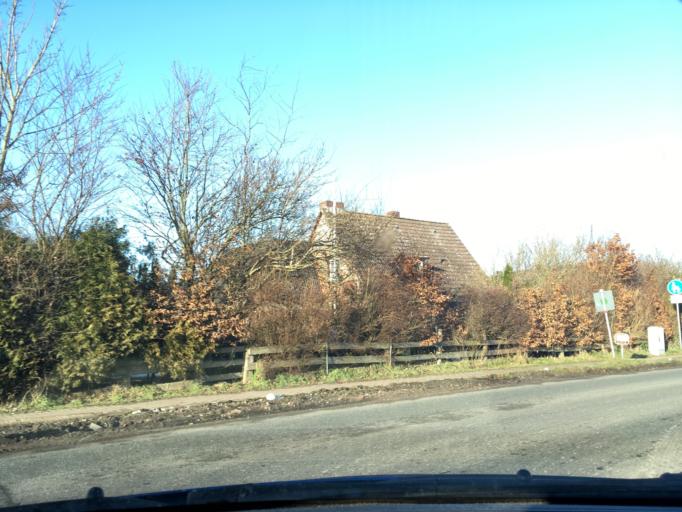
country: DE
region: Schleswig-Holstein
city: Gulzow
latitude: 53.4398
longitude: 10.4826
